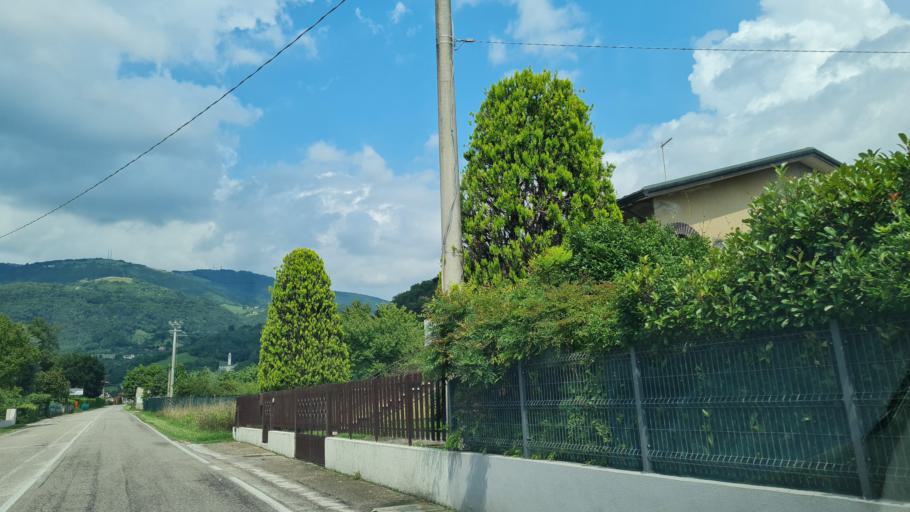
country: IT
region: Veneto
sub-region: Provincia di Vicenza
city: Marostica
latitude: 45.7593
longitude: 11.6607
